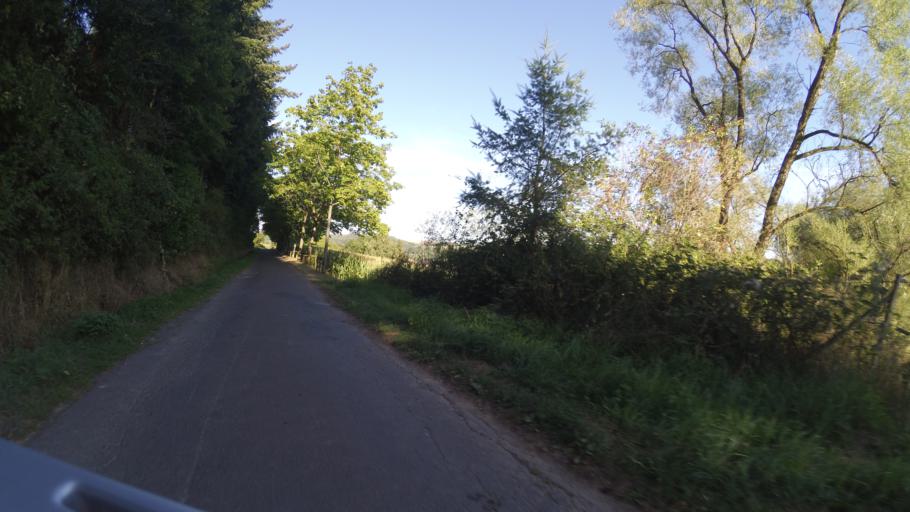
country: DE
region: Saarland
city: Eppelborn
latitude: 49.4449
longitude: 6.9502
